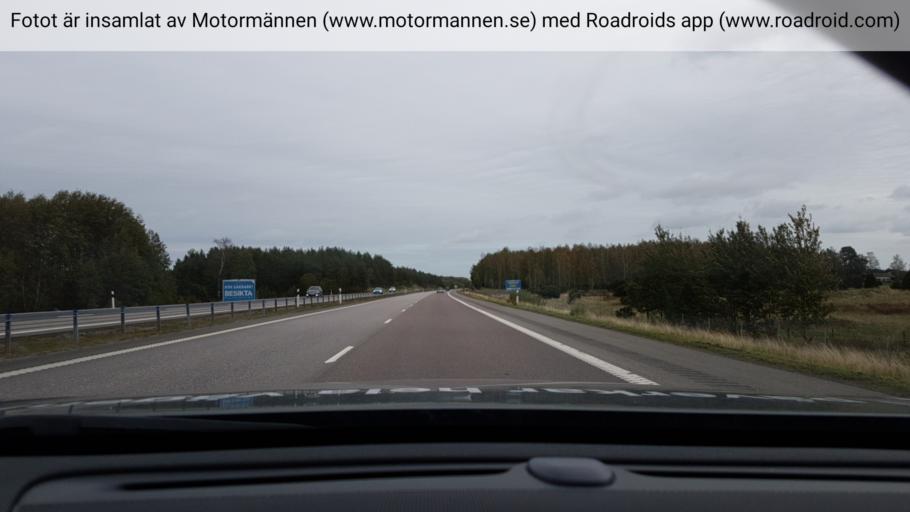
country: SE
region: OEstergoetland
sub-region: Linkopings Kommun
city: Vikingstad
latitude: 58.3834
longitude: 15.3654
